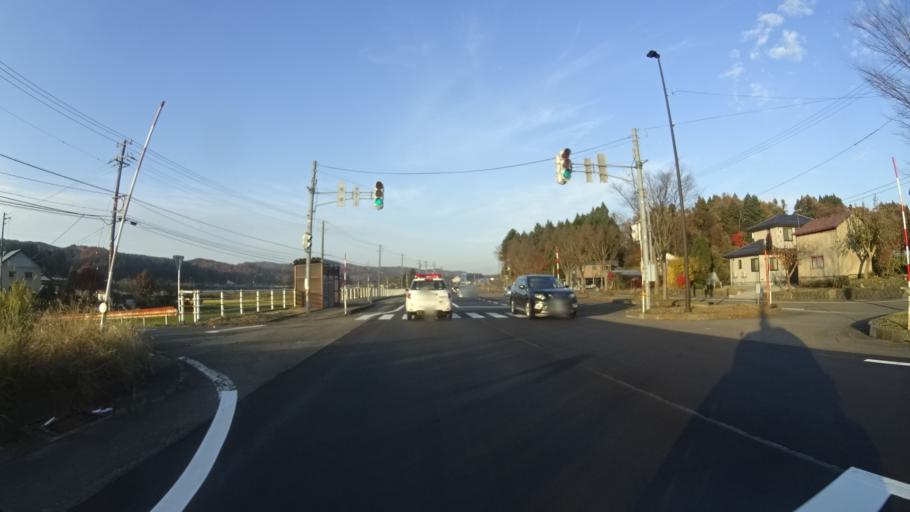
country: JP
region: Niigata
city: Nagaoka
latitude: 37.4444
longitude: 138.7429
